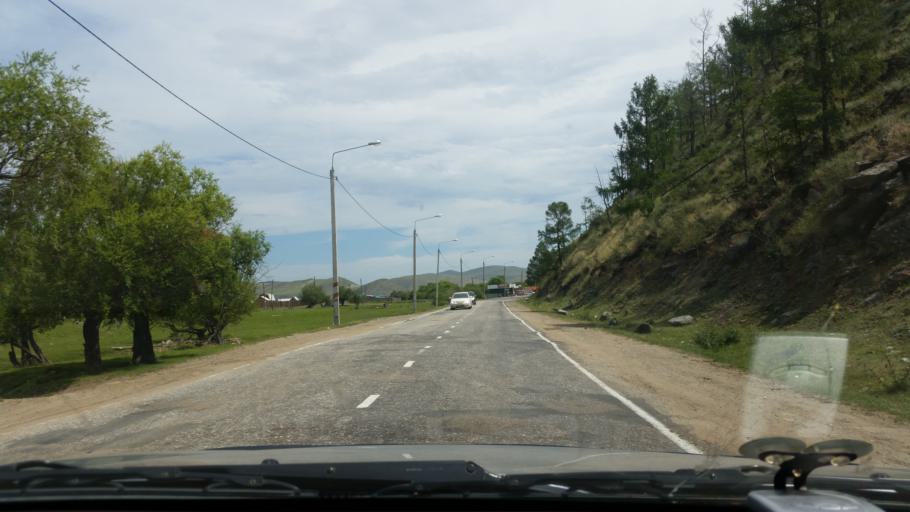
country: RU
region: Irkutsk
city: Yelantsy
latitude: 52.7993
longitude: 106.4194
